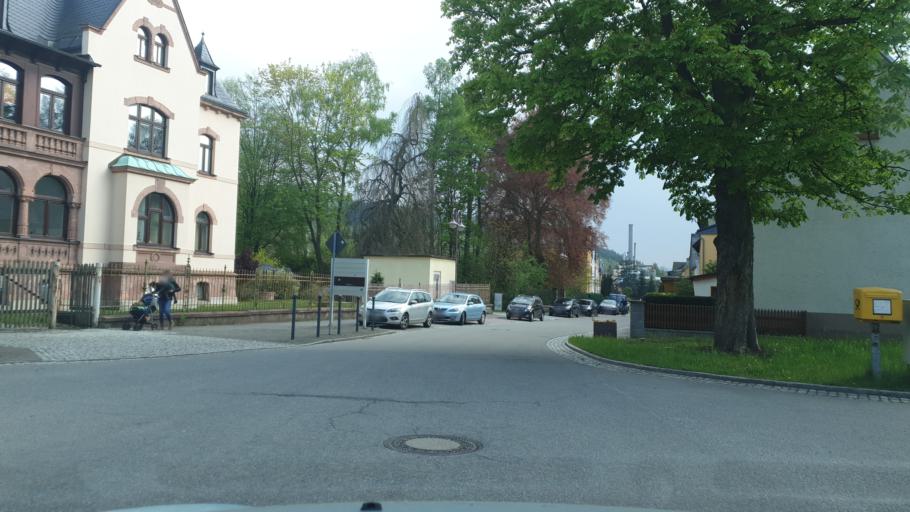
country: DE
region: Saxony
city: Lossnitz
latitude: 50.6177
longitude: 12.7280
